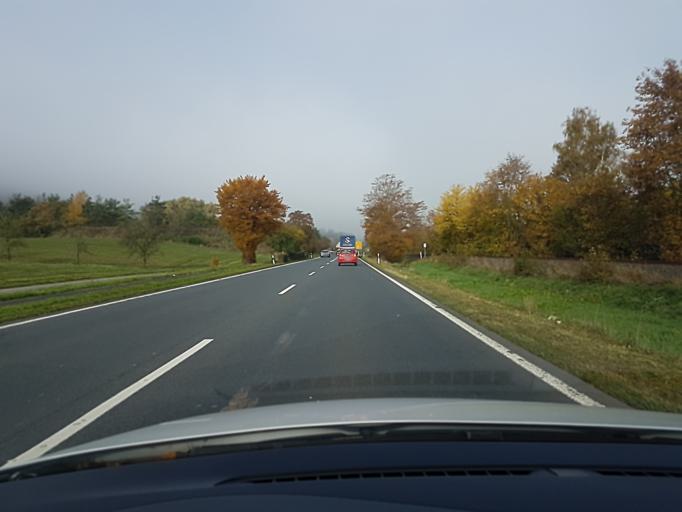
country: DE
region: Bavaria
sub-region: Regierungsbezirk Unterfranken
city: Laudenbach
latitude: 49.7351
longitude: 9.1863
